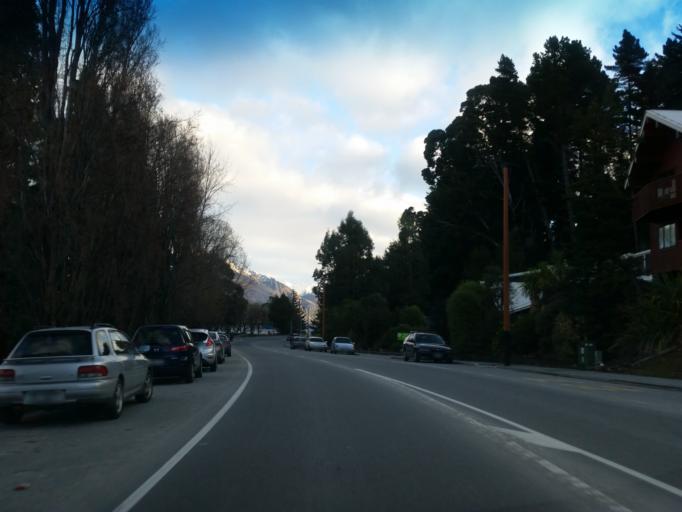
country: NZ
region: Otago
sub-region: Queenstown-Lakes District
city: Queenstown
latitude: -45.0361
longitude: 168.6504
